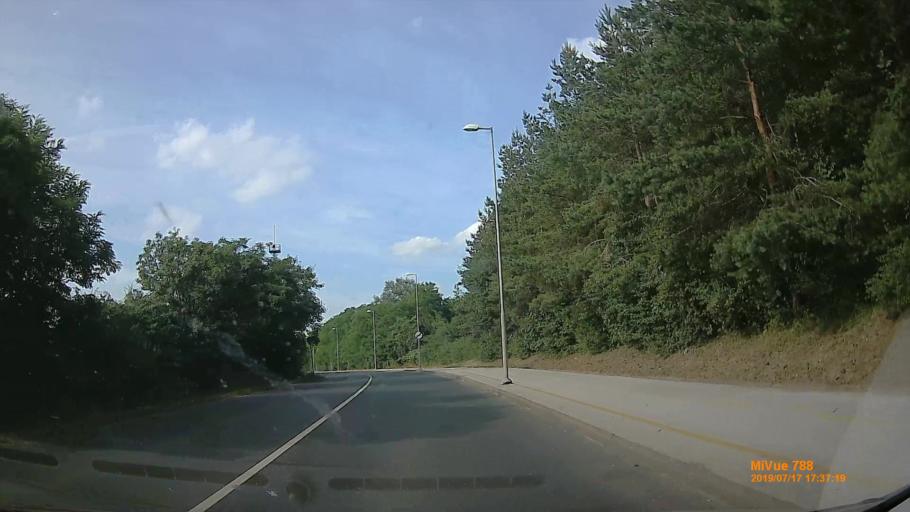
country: HU
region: Veszprem
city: Ajka
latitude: 47.0791
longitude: 17.5476
